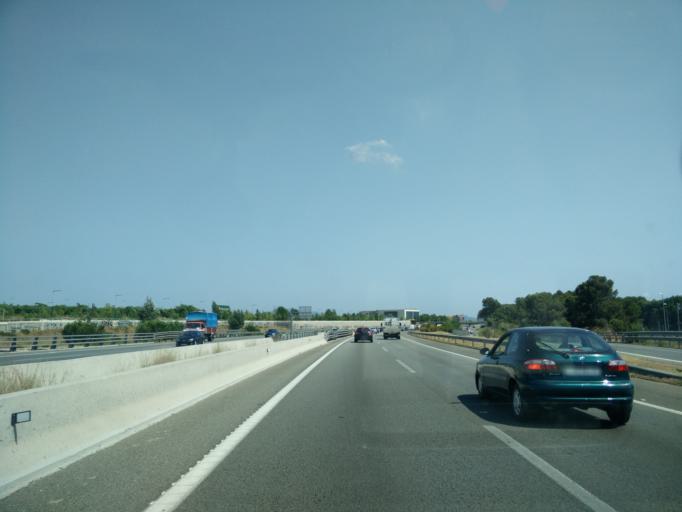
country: ES
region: Catalonia
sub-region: Provincia de Barcelona
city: Sant Quirze del Valles
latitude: 41.5412
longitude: 2.0810
